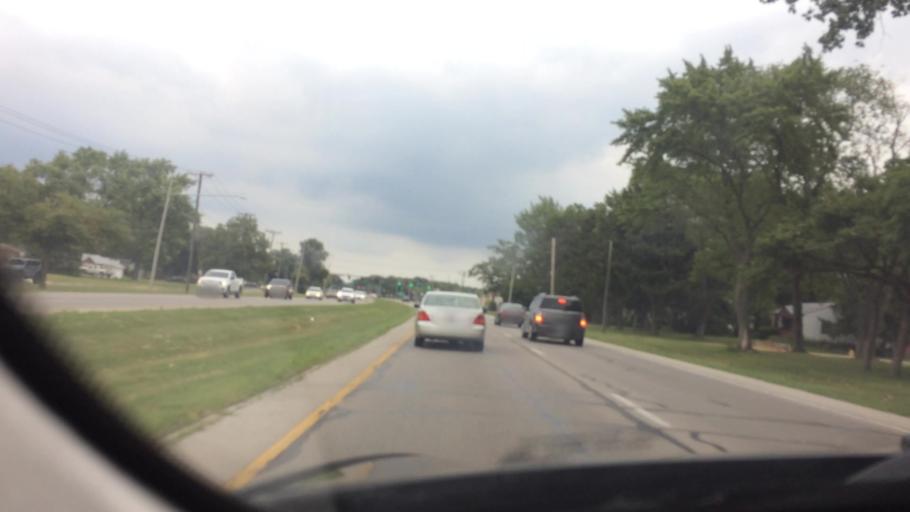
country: US
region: Ohio
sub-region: Wood County
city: Perrysburg
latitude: 41.5801
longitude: -83.6248
